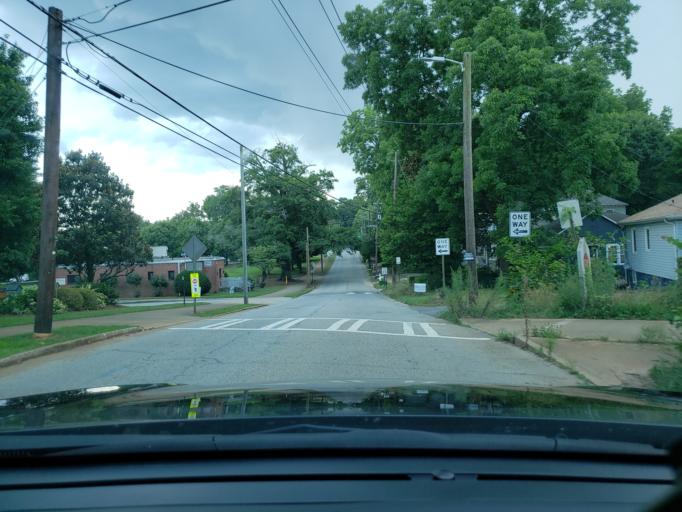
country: US
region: Georgia
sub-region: DeKalb County
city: Druid Hills
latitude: 33.7550
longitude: -84.3292
